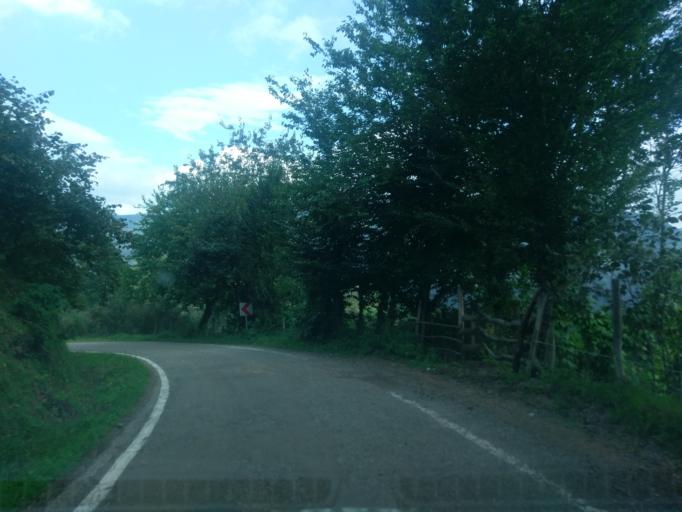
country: TR
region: Ordu
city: Camas
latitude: 40.9257
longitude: 37.6092
